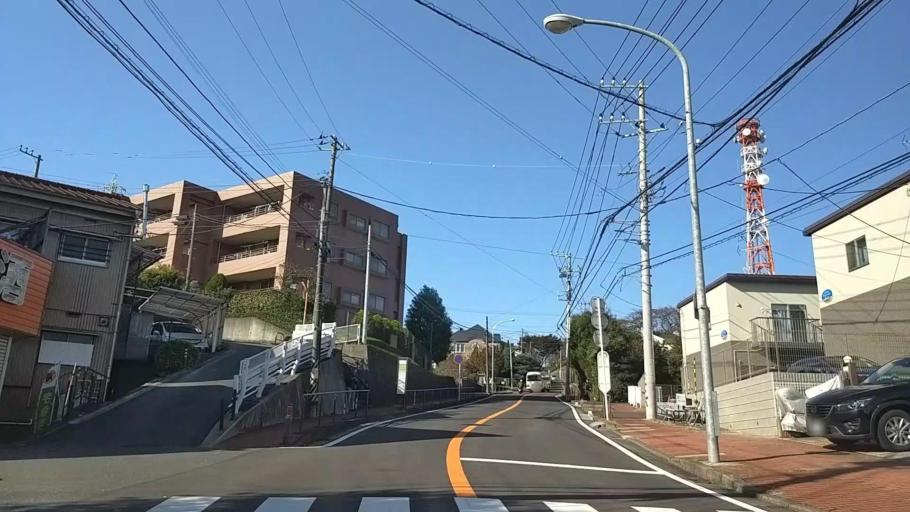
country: JP
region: Kanagawa
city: Yokohama
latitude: 35.4655
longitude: 139.5752
